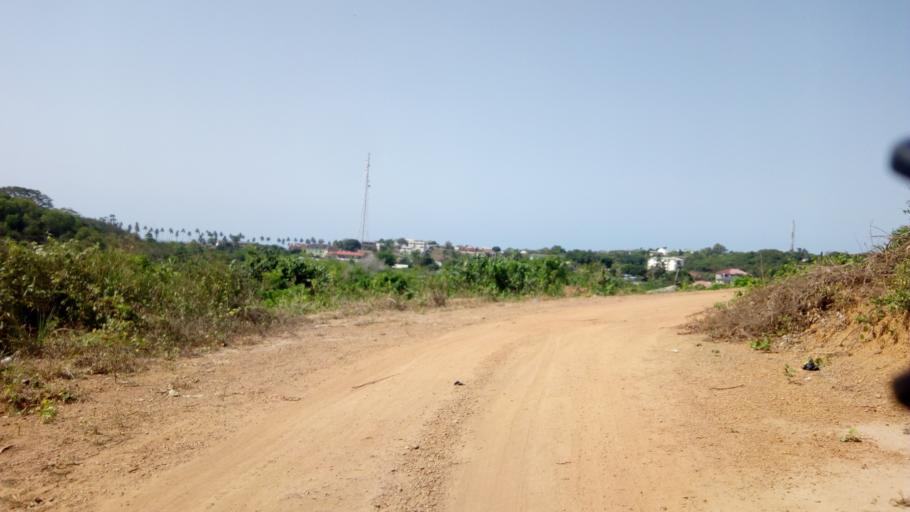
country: GH
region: Central
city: Cape Coast
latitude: 5.1104
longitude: -1.2676
